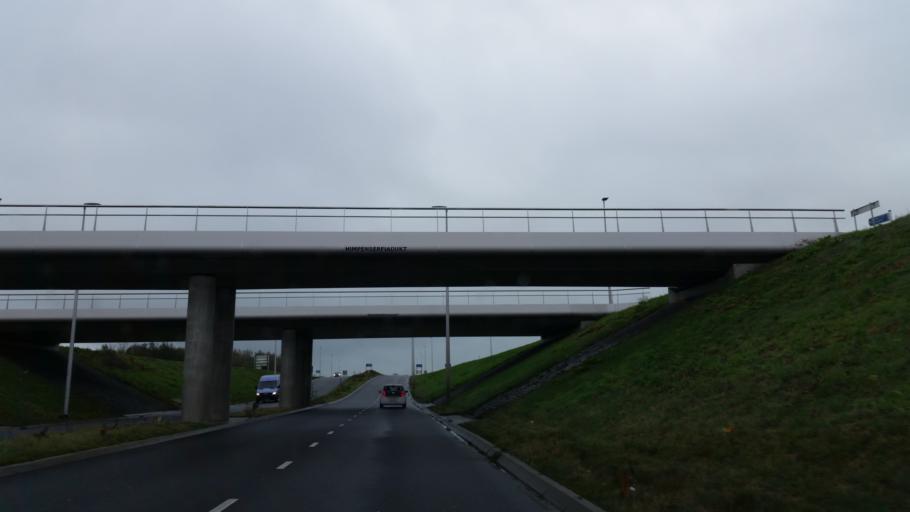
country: NL
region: Friesland
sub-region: Gemeente Leeuwarden
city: Huizum
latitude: 53.1807
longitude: 5.8212
